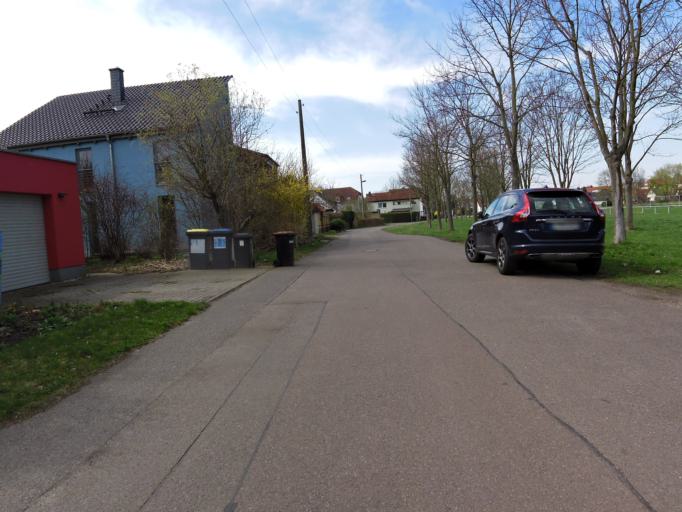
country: DE
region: Saxony
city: Schkeuditz
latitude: 51.3814
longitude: 12.2799
